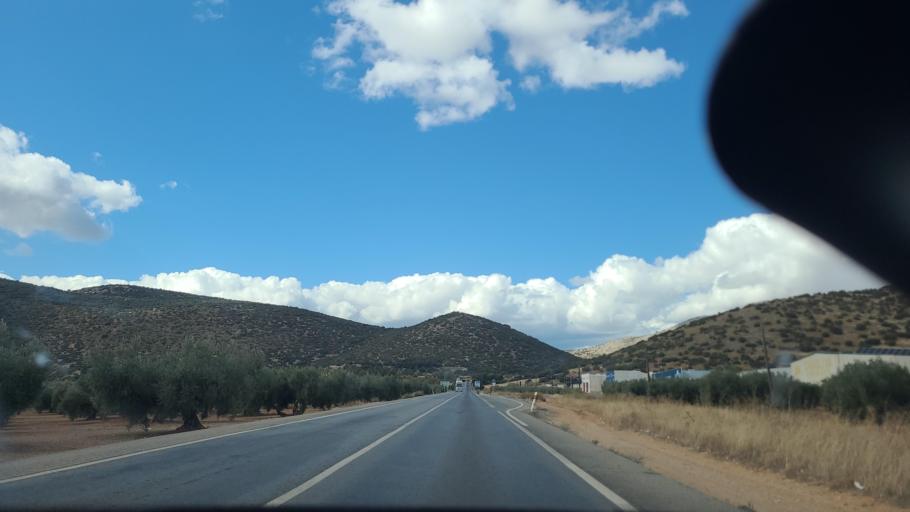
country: ES
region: Andalusia
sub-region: Provincia de Granada
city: Iznalloz
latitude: 37.4022
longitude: -3.5570
